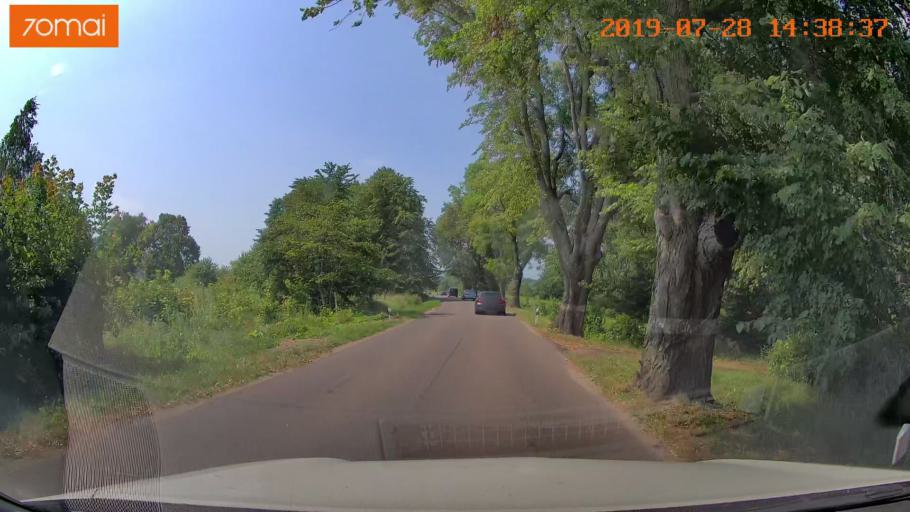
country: RU
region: Kaliningrad
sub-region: Gorod Kaliningrad
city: Yantarnyy
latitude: 54.8454
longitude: 19.9814
